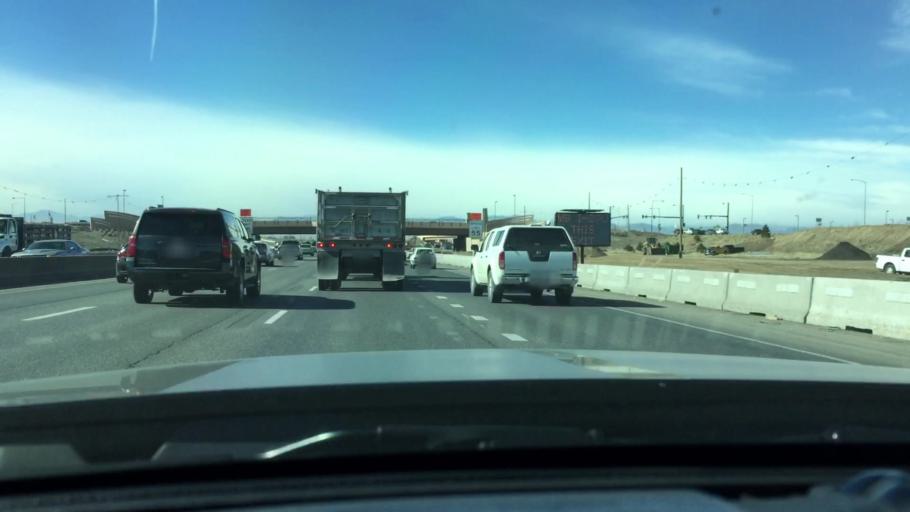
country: US
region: Colorado
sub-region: Adams County
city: Commerce City
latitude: 39.7782
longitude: -104.8789
